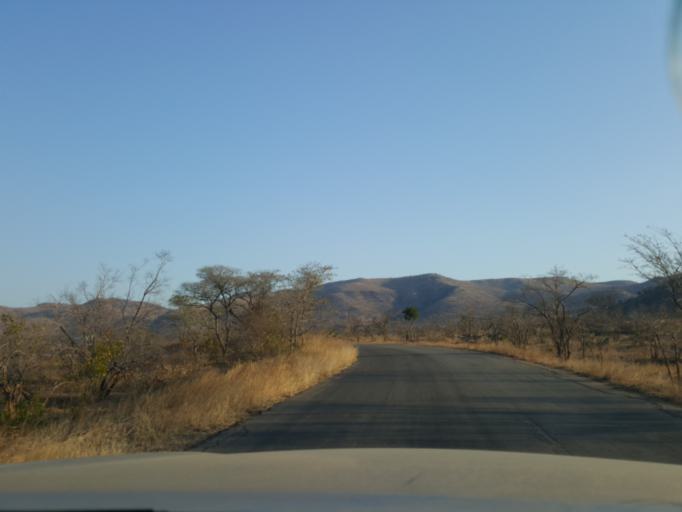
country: SZ
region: Hhohho
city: Ntfonjeni
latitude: -25.4381
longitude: 31.4449
